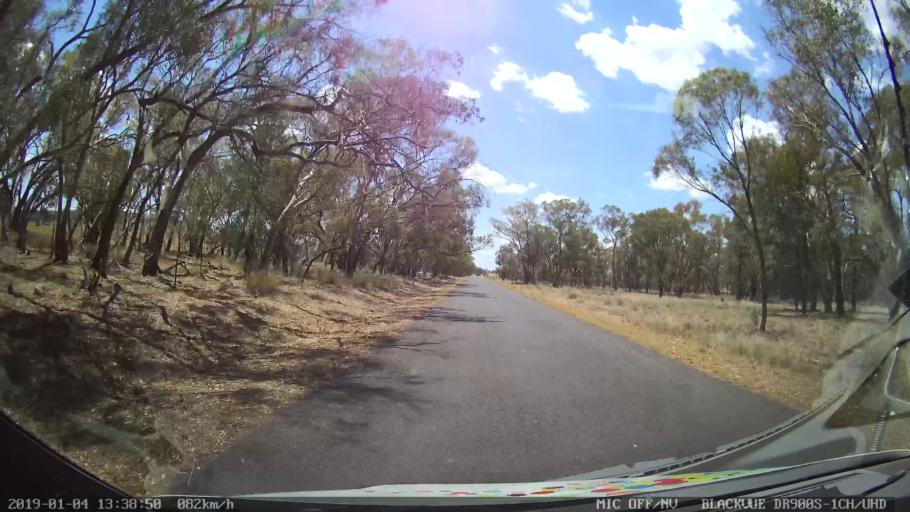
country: AU
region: New South Wales
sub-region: Dubbo Municipality
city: Dubbo
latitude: -32.5332
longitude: 148.5497
